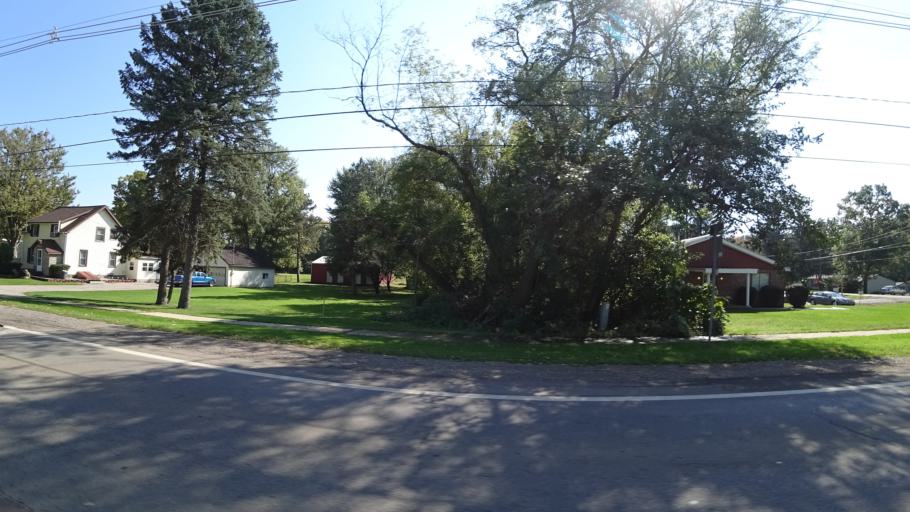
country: US
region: Michigan
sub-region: Jackson County
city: Spring Arbor
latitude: 42.2042
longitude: -84.5580
